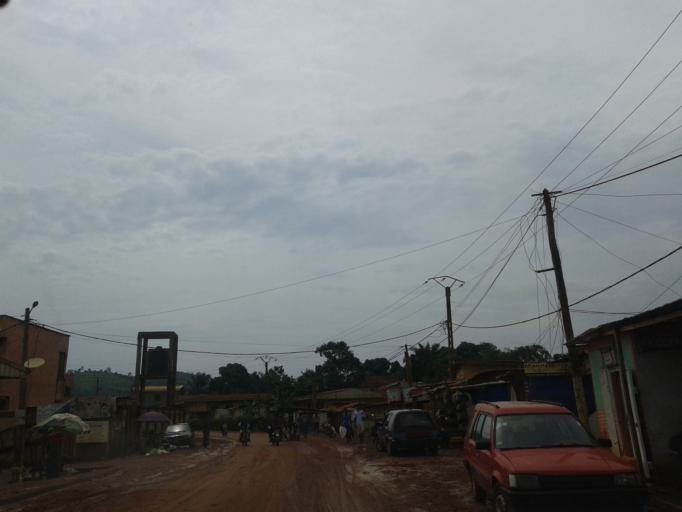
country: CM
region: Centre
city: Yaounde
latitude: 3.9232
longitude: 11.5187
